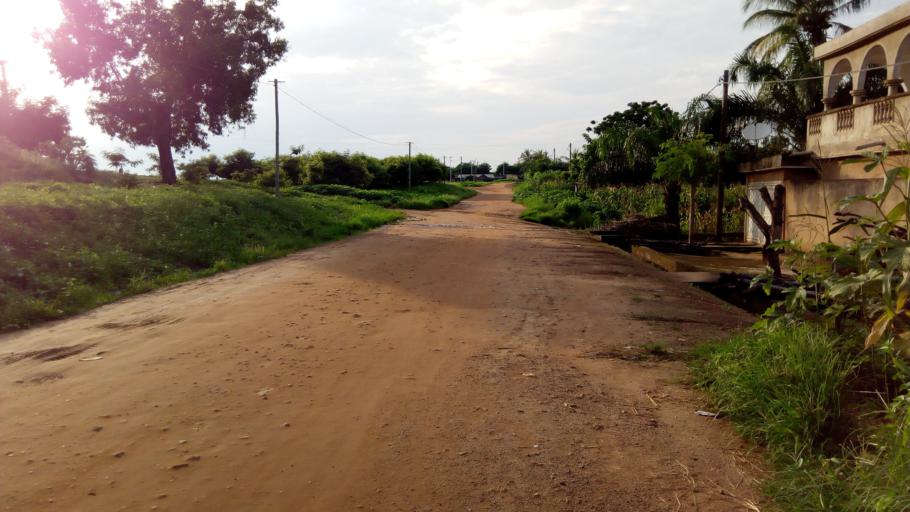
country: TG
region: Kara
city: Kara
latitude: 9.5618
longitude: 1.2073
